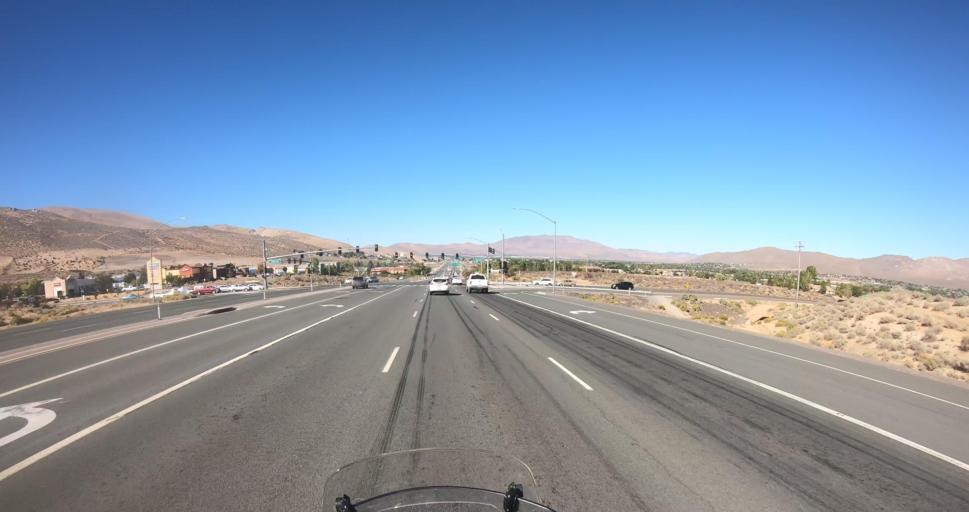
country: US
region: Nevada
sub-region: Douglas County
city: Indian Hills
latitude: 39.1092
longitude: -119.7730
